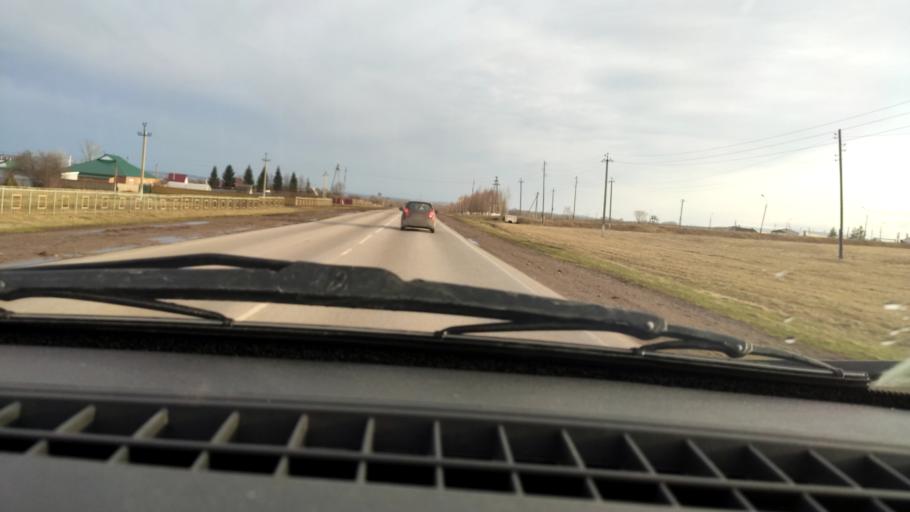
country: RU
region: Bashkortostan
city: Davlekanovo
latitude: 54.3793
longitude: 55.1956
